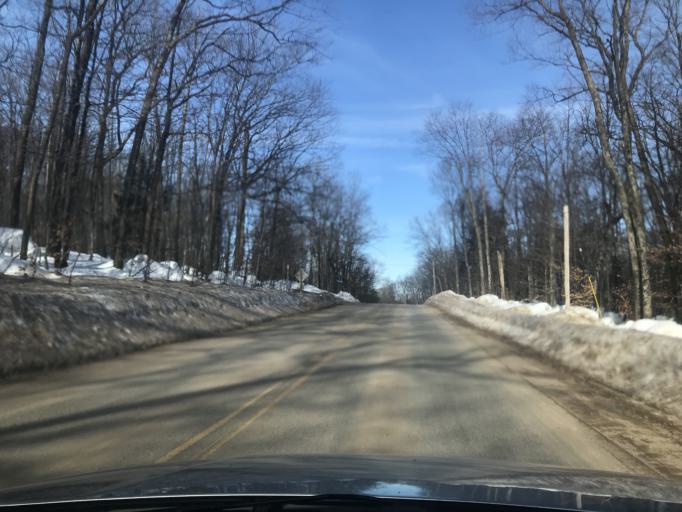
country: US
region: Michigan
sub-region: Dickinson County
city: Kingsford
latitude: 45.4058
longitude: -88.3478
